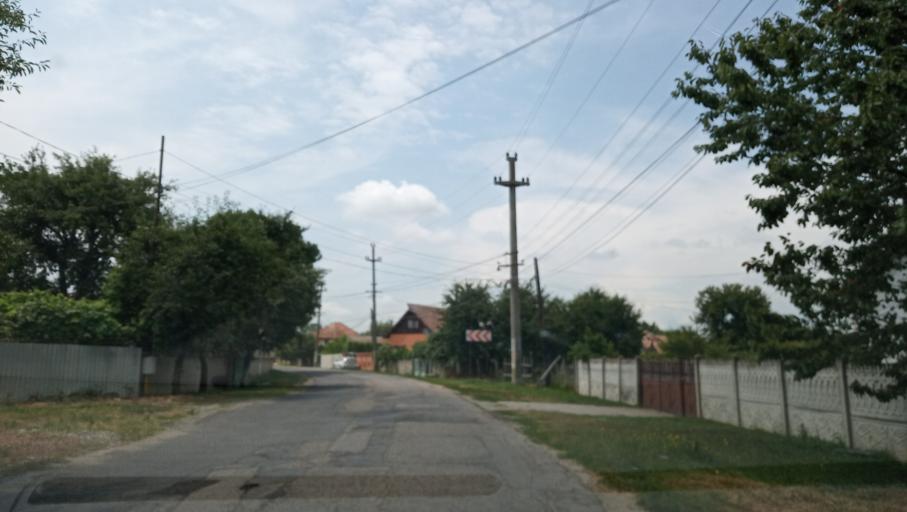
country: RO
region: Gorj
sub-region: Comuna Turcinesti
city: Turcinesti
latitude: 45.1137
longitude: 23.3224
